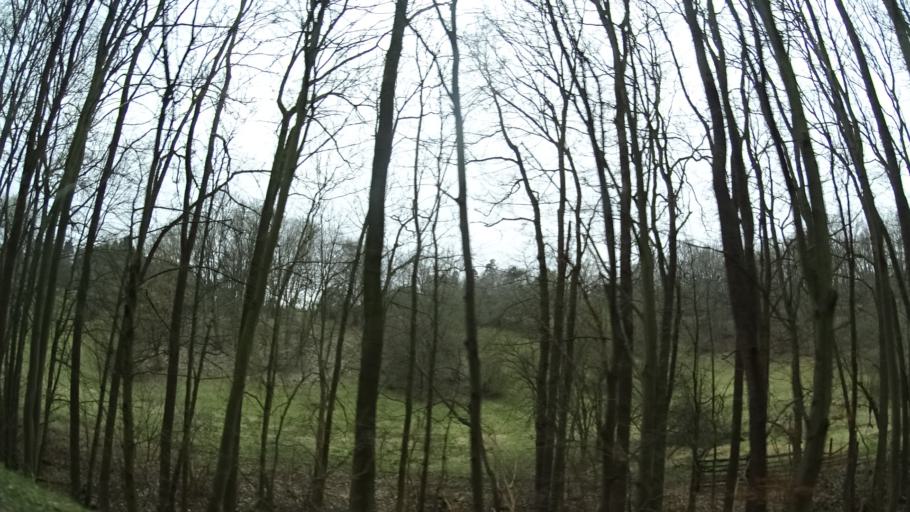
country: DE
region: Thuringia
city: Bad Blankenburg
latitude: 50.6986
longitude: 11.2282
